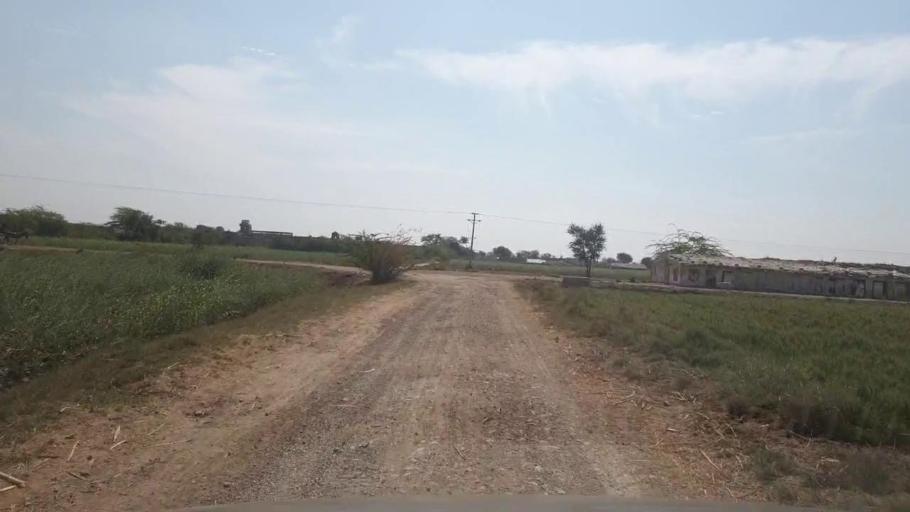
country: PK
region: Sindh
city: Mirwah Gorchani
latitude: 25.4363
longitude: 69.1933
